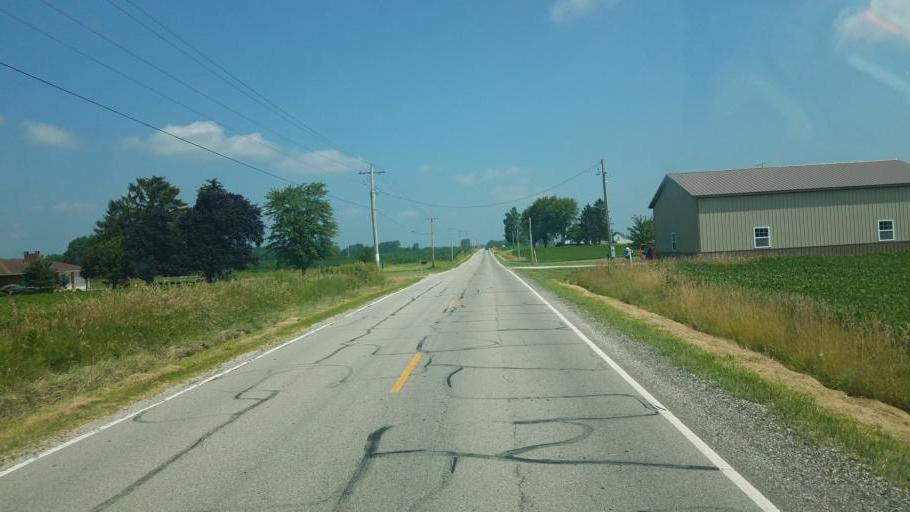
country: US
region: Ohio
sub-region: Huron County
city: Willard
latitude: 40.9745
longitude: -82.8534
